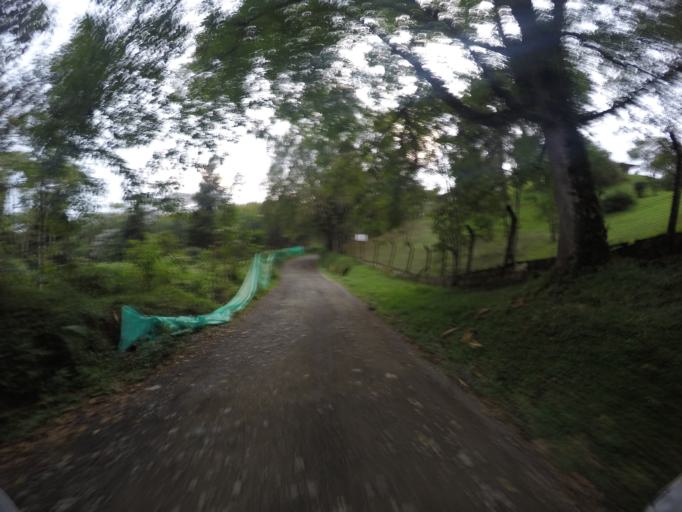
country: CO
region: Quindio
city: Filandia
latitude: 4.7139
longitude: -75.6362
